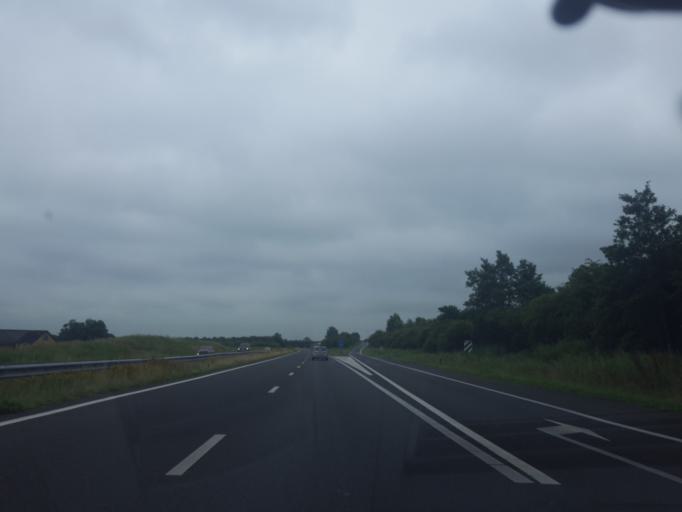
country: NL
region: Friesland
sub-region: Gemeente Boarnsterhim
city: Reduzum
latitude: 53.1175
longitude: 5.8098
